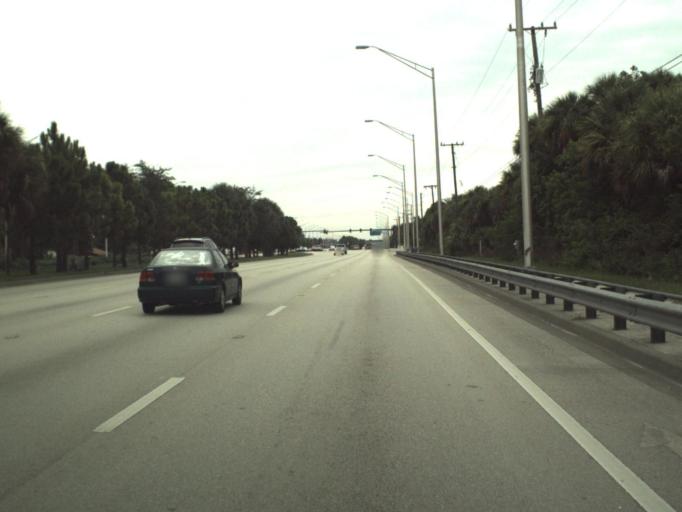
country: US
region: Florida
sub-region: Palm Beach County
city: Lake Belvedere Estates
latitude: 26.6795
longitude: -80.1776
